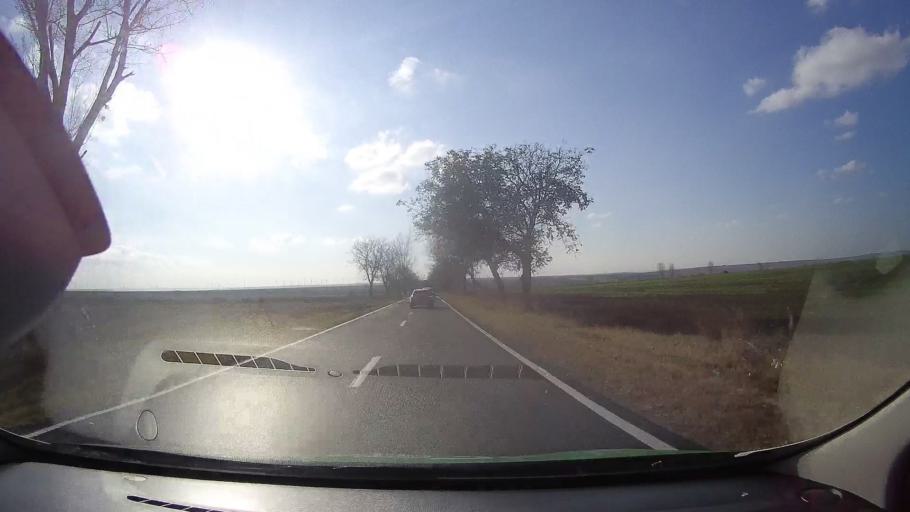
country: RO
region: Tulcea
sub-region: Comuna Topolog
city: Topolog
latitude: 44.8497
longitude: 28.3228
